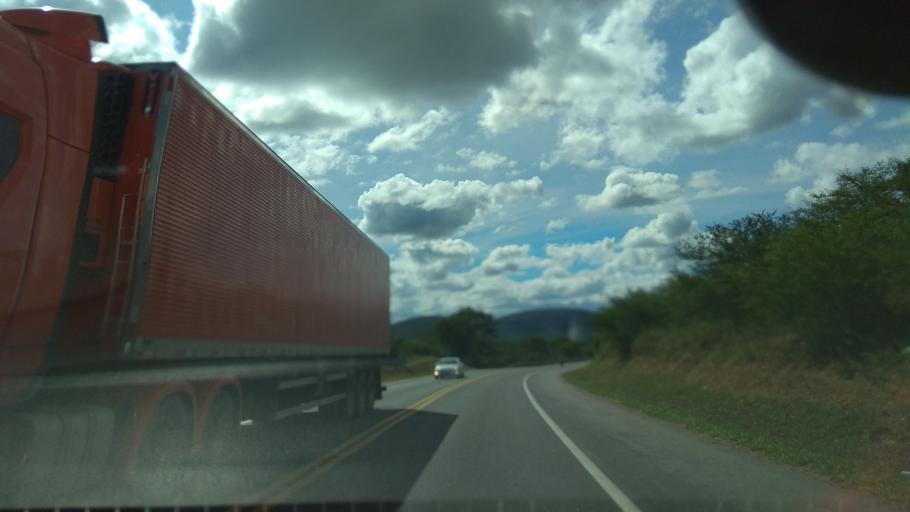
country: BR
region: Bahia
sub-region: Santa Ines
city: Santa Ines
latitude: -13.3060
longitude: -40.0263
